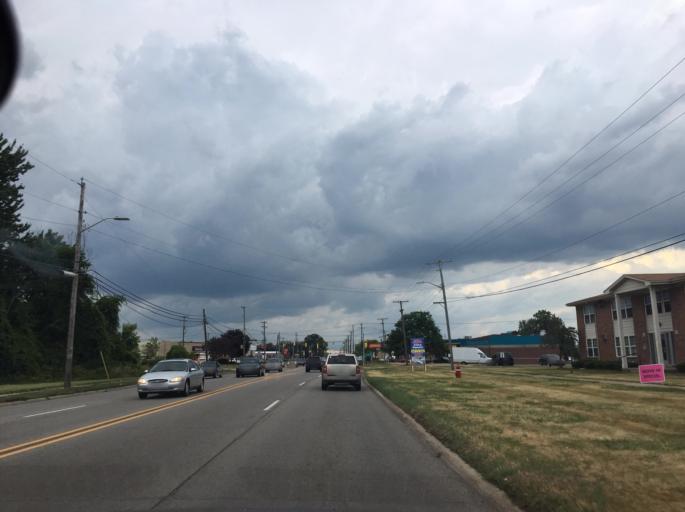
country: US
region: Michigan
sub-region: Macomb County
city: Fraser
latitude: 42.5226
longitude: -82.9434
